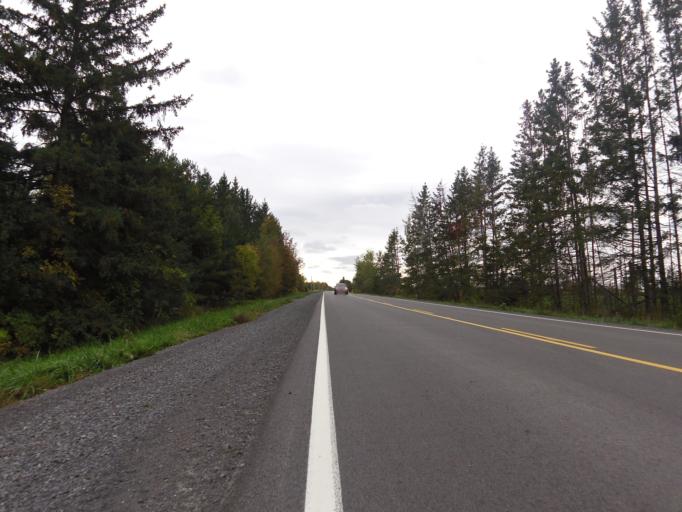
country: CA
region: Ontario
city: Arnprior
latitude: 45.4891
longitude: -76.1909
